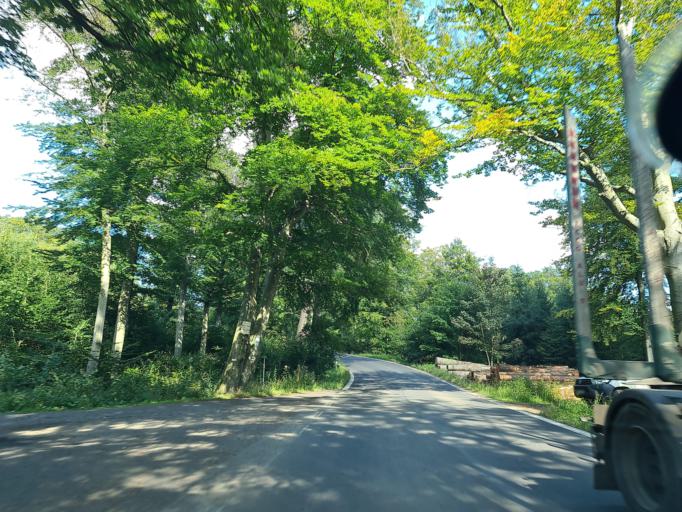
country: CZ
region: Ustecky
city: Mezibori
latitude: 50.6011
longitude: 13.5911
